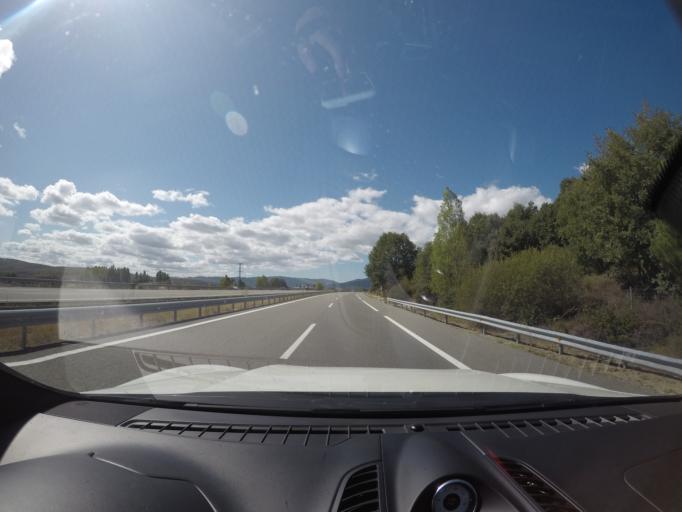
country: ES
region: Castille and Leon
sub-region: Provincia de Zamora
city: Puebla de Sanabria
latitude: 42.0623
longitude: -6.6375
